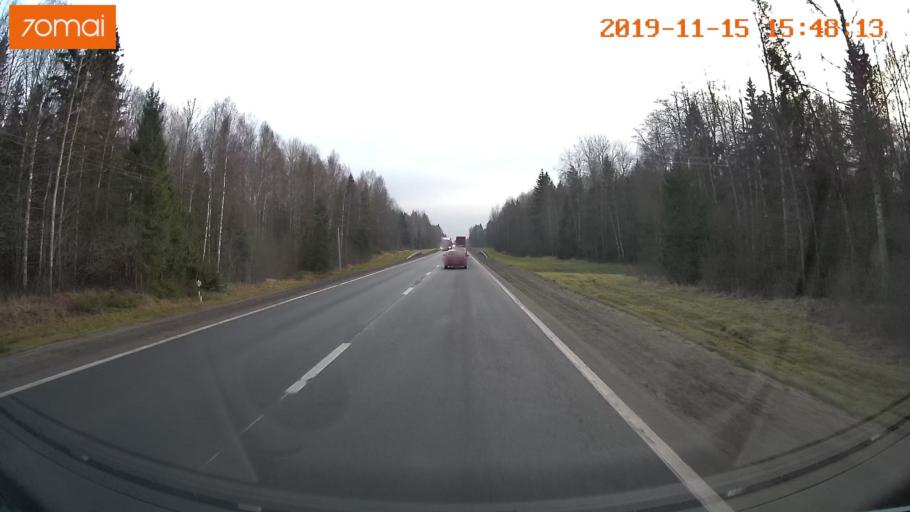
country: RU
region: Jaroslavl
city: Danilov
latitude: 57.9298
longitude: 40.0065
